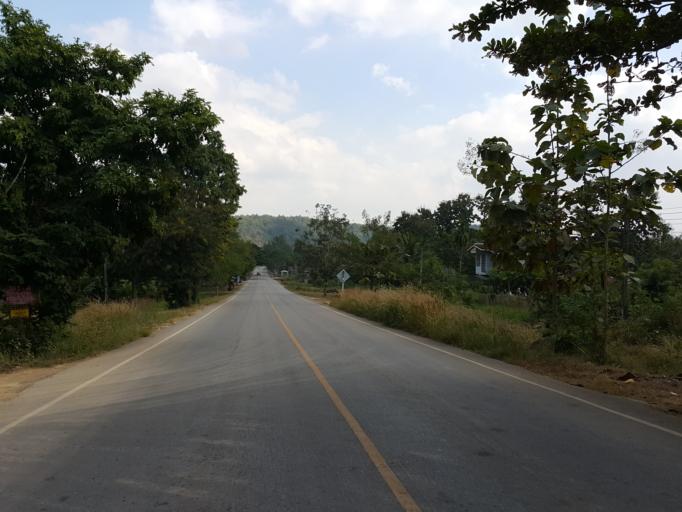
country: TH
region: Sukhothai
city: Thung Saliam
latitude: 17.3425
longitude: 99.4617
